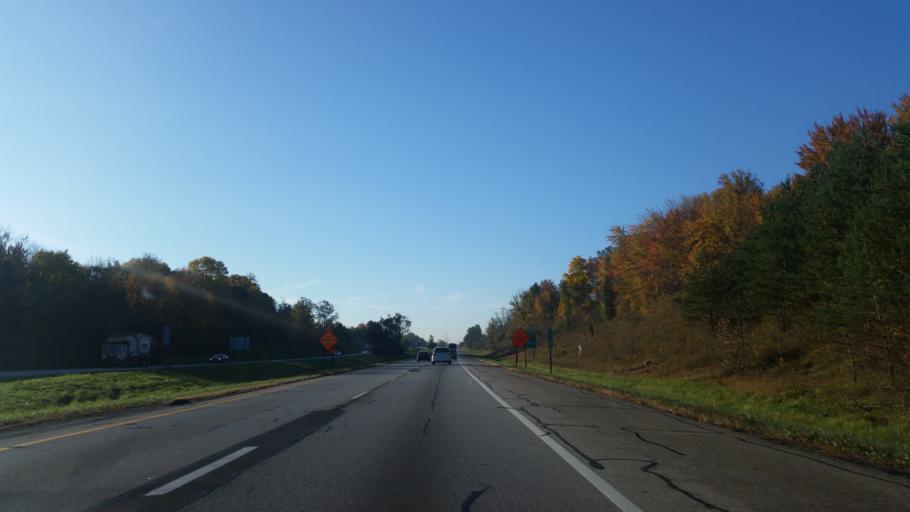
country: US
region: Ohio
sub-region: Summit County
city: Richfield
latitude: 41.2486
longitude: -81.6296
